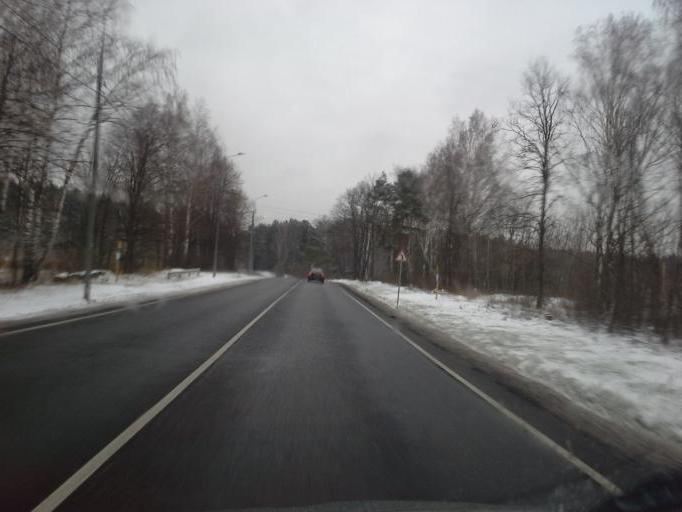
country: RU
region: Moskovskaya
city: Nikolina Gora
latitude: 55.7138
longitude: 37.0807
